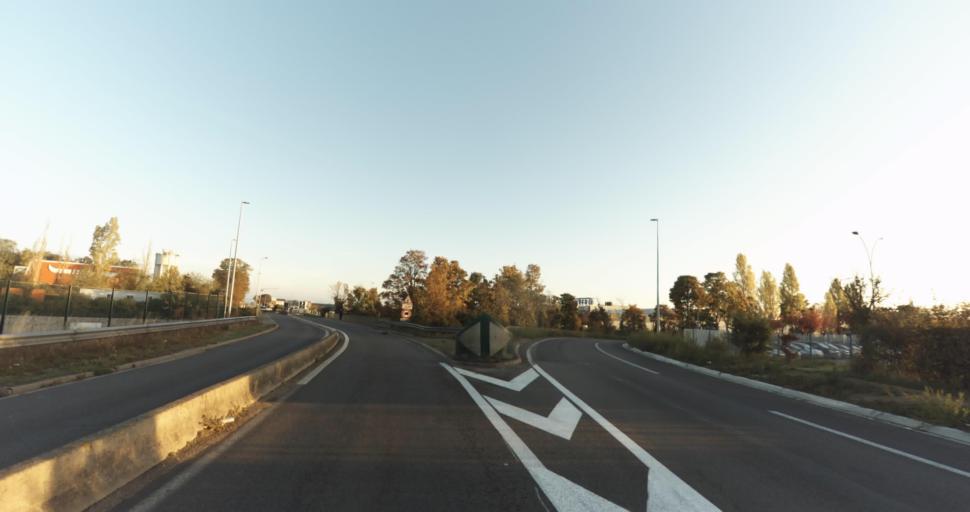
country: FR
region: Centre
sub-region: Departement d'Eure-et-Loir
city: Vernouillet
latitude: 48.7144
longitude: 1.3678
